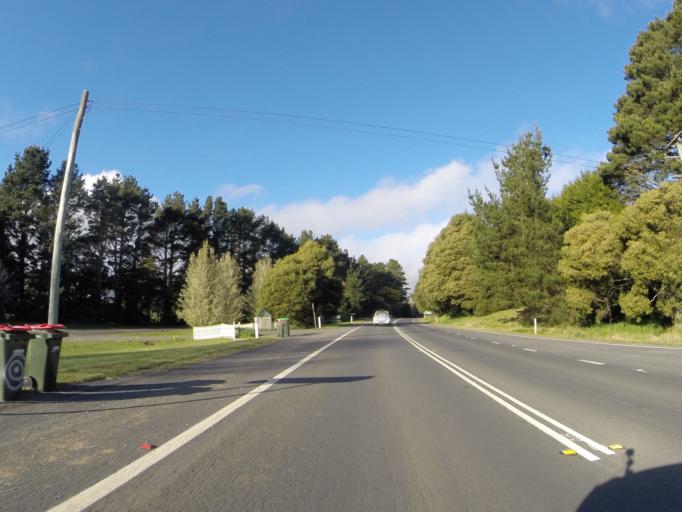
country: AU
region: New South Wales
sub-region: Shellharbour
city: Calderwood
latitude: -34.5881
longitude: 150.5793
